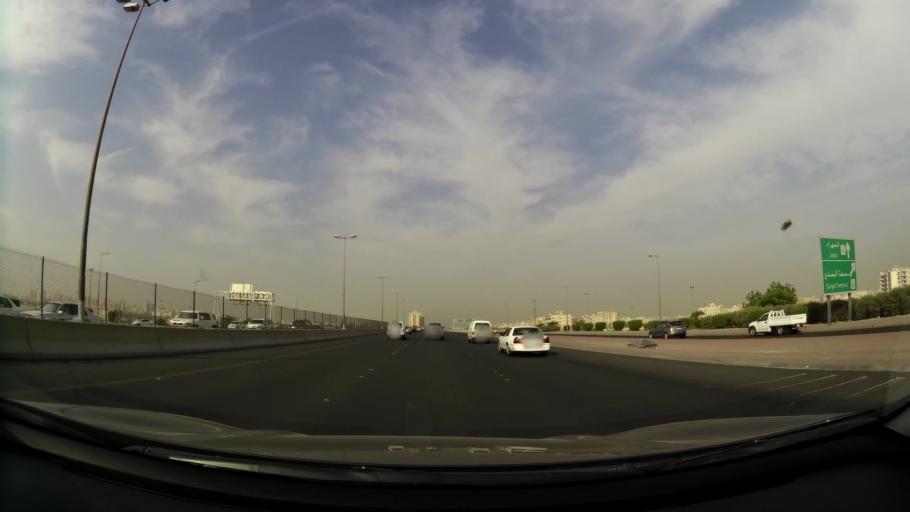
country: KW
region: Al Farwaniyah
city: Al Farwaniyah
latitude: 29.2661
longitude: 47.9541
